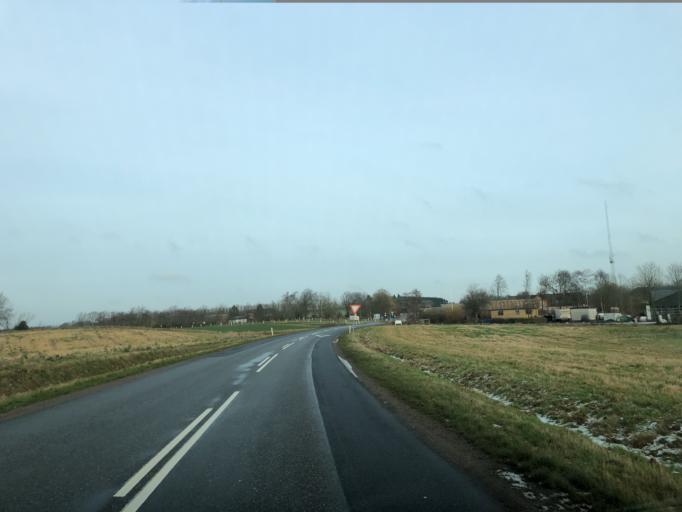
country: DK
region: Central Jutland
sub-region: Hedensted Kommune
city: Torring
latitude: 55.8052
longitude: 9.4582
